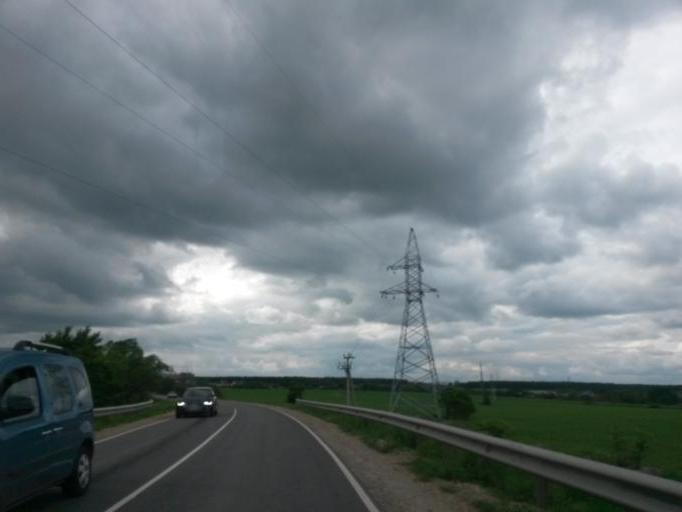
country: RU
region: Moskovskaya
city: Klimovsk
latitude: 55.3444
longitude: 37.5853
